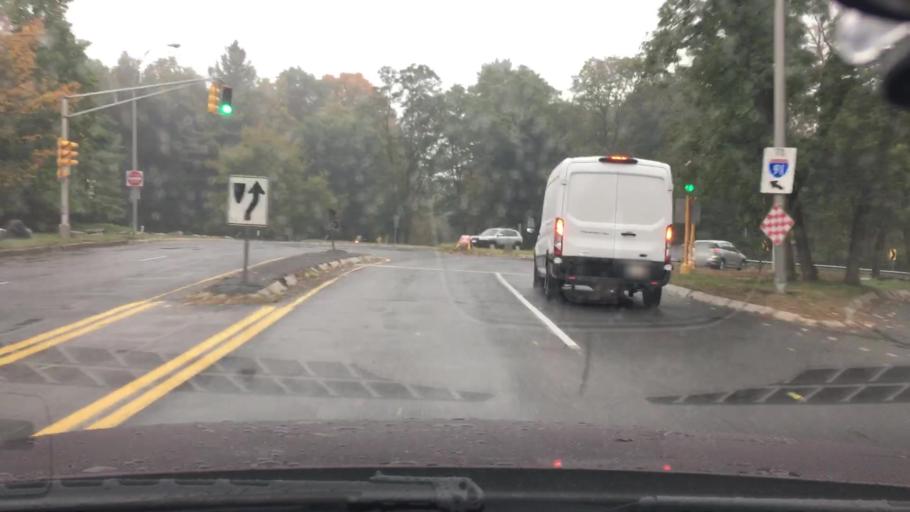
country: US
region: Massachusetts
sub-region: Hampden County
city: Springfield
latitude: 42.0791
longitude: -72.5753
